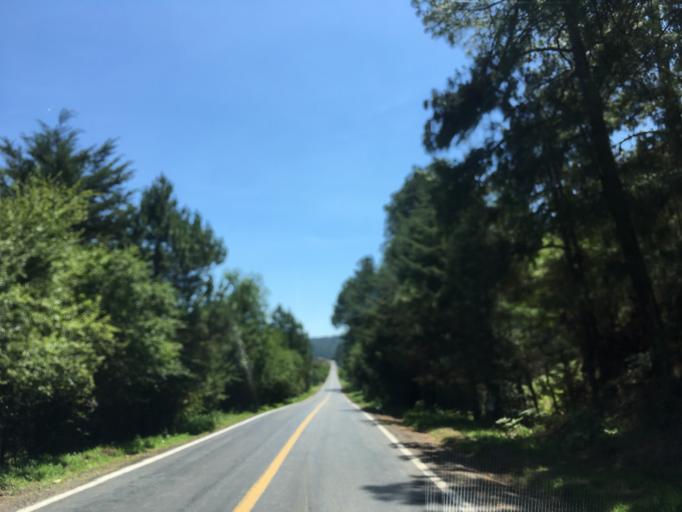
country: MX
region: Michoacan
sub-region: Hidalgo
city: Tierras Coloradas (San Pedro)
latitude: 19.6674
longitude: -100.7472
